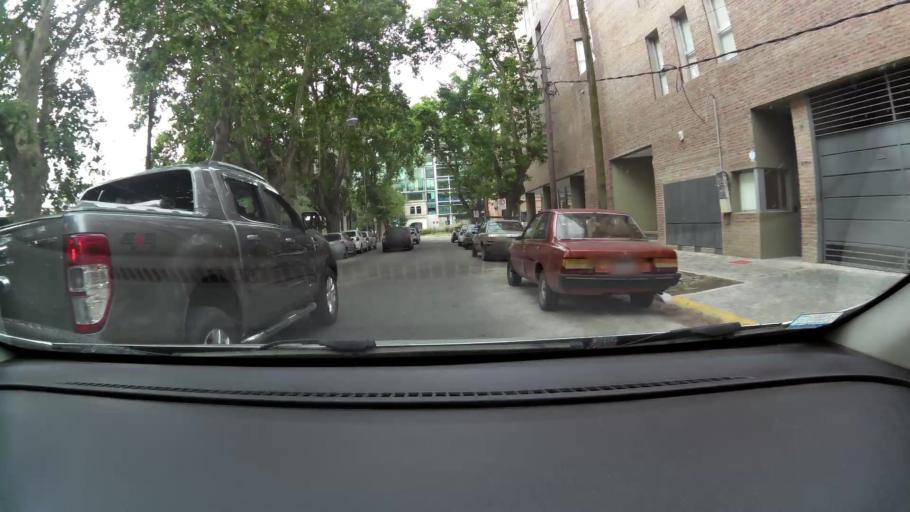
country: AR
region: Santa Fe
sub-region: Departamento de Rosario
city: Rosario
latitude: -32.9241
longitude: -60.6654
